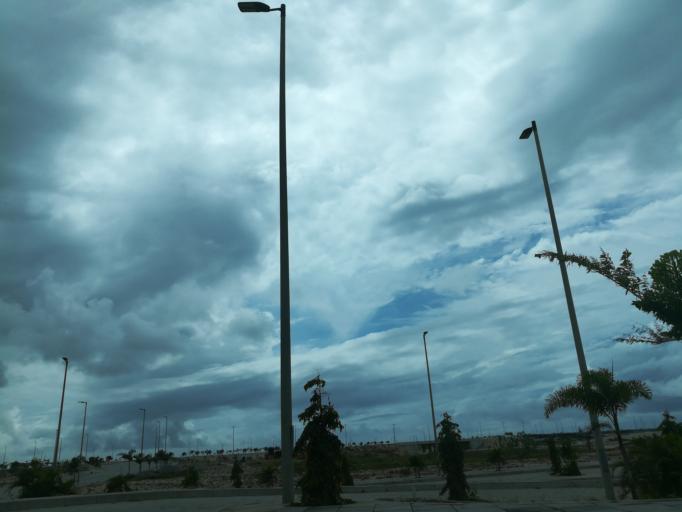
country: NG
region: Lagos
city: Lagos
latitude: 6.4146
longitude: 3.4114
